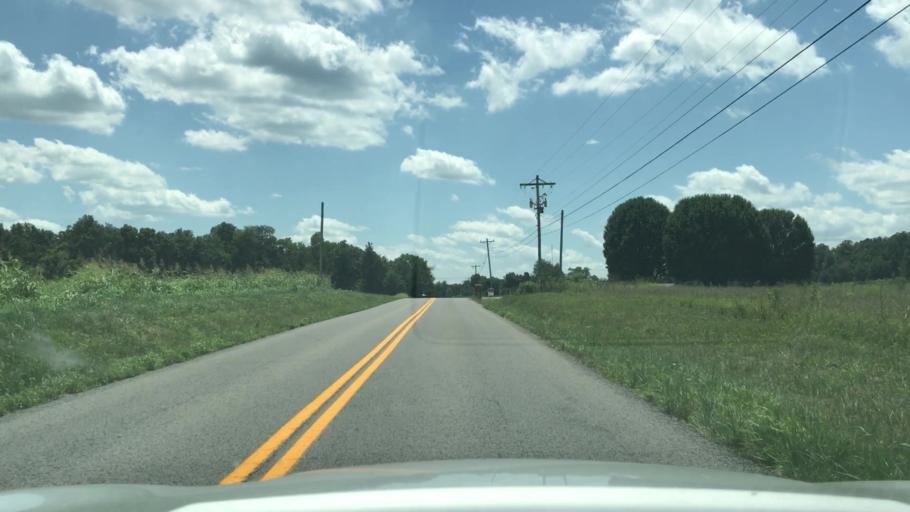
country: US
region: Kentucky
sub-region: Christian County
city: Hopkinsville
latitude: 36.9780
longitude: -87.3644
